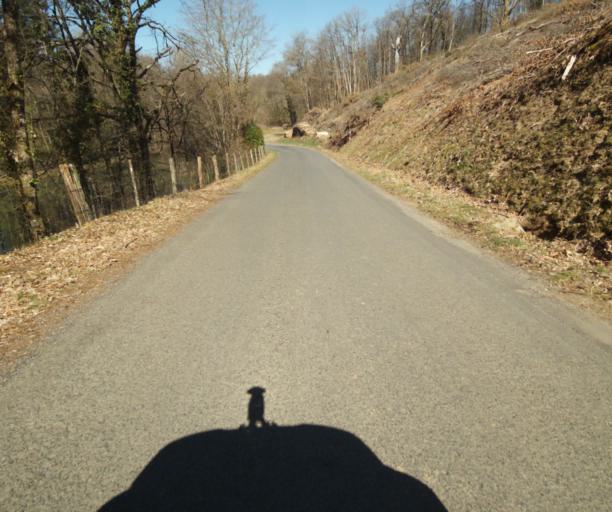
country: FR
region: Limousin
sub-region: Departement de la Correze
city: Saint-Clement
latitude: 45.3408
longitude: 1.6452
